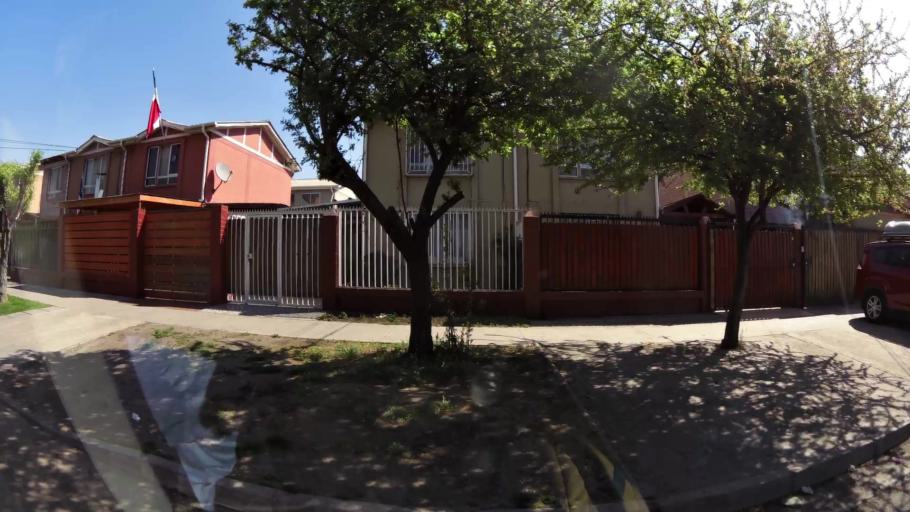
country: CL
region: Santiago Metropolitan
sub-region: Provincia de Santiago
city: Lo Prado
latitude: -33.3510
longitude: -70.7342
